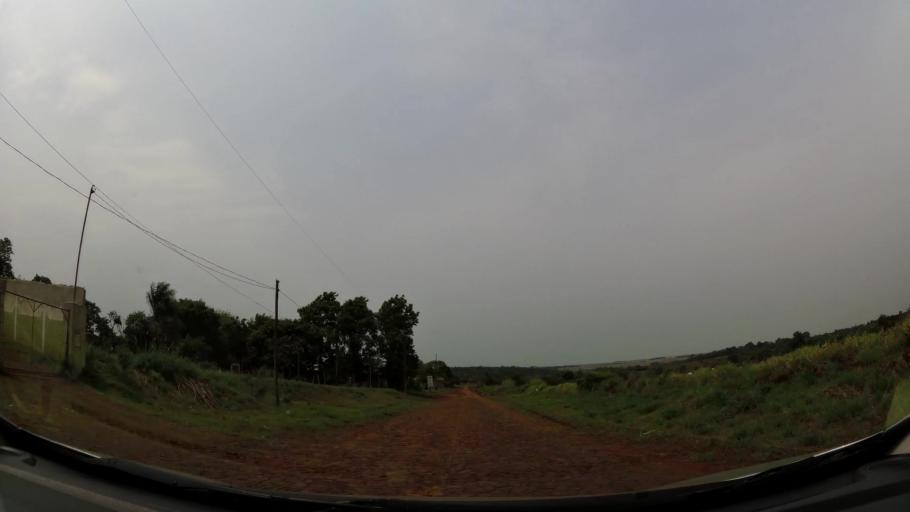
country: PY
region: Alto Parana
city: Presidente Franco
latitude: -25.5572
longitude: -54.6411
